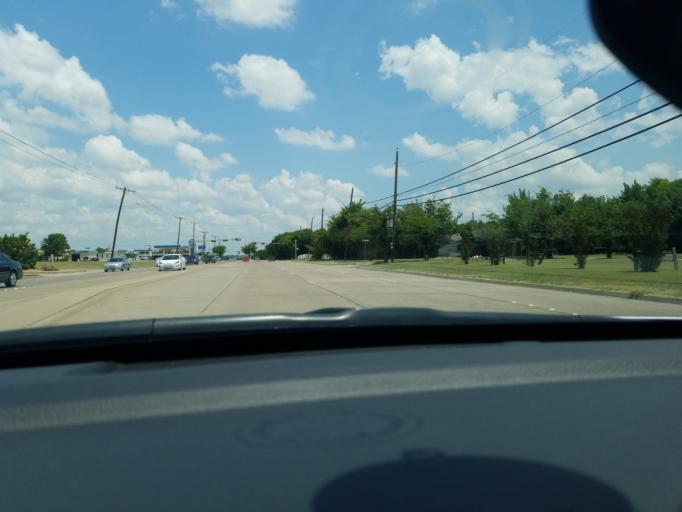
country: US
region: Texas
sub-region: Dallas County
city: Sunnyvale
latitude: 32.8212
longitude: -96.5958
